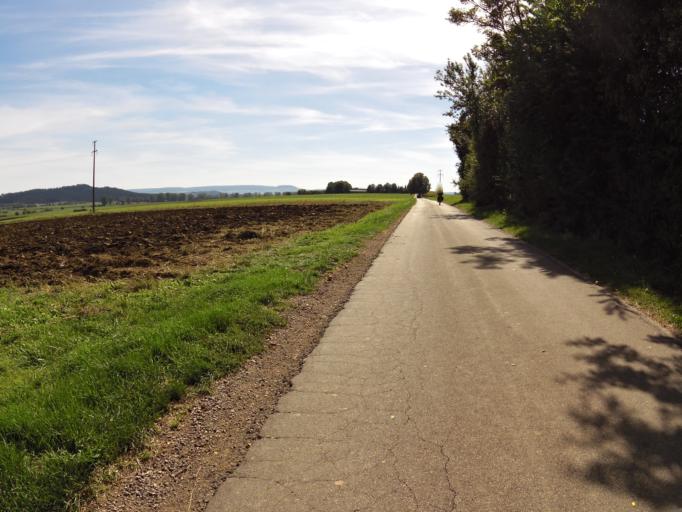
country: DE
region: Baden-Wuerttemberg
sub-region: Freiburg Region
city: Bad Durrheim
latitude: 48.0031
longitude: 8.5025
